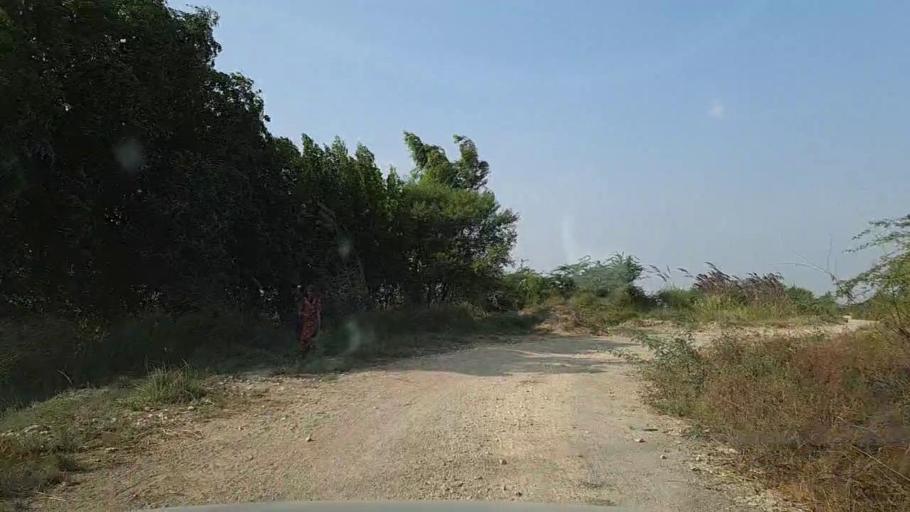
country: PK
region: Sindh
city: Mirpur Sakro
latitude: 24.5797
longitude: 67.5678
